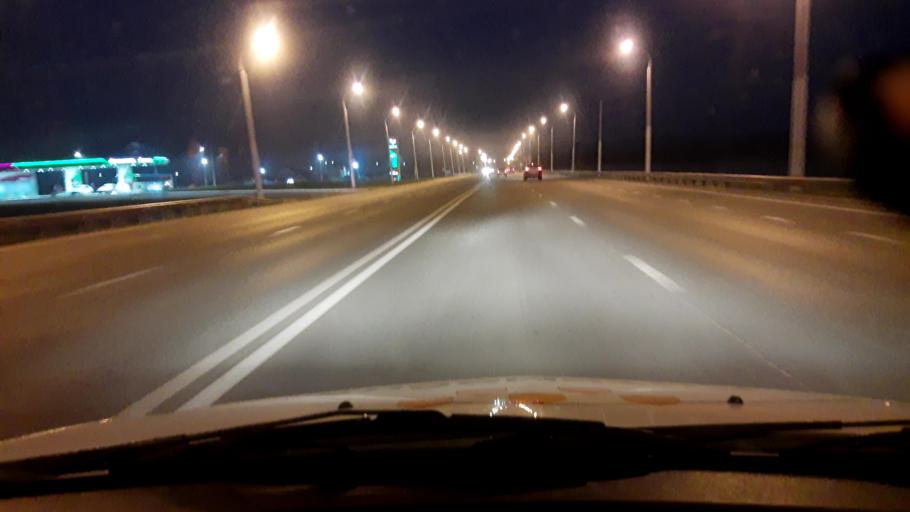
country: RU
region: Bashkortostan
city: Ufa
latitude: 54.8055
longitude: 56.1798
